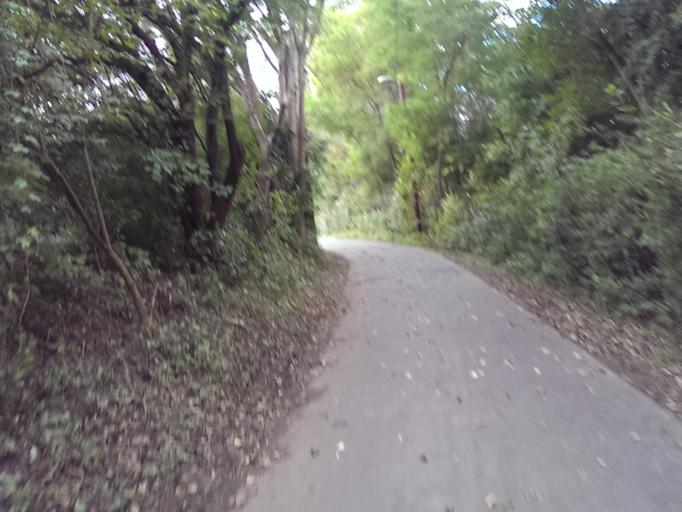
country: AT
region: Styria
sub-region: Politischer Bezirk Graz-Umgebung
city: Raaba
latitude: 47.0364
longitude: 15.4761
